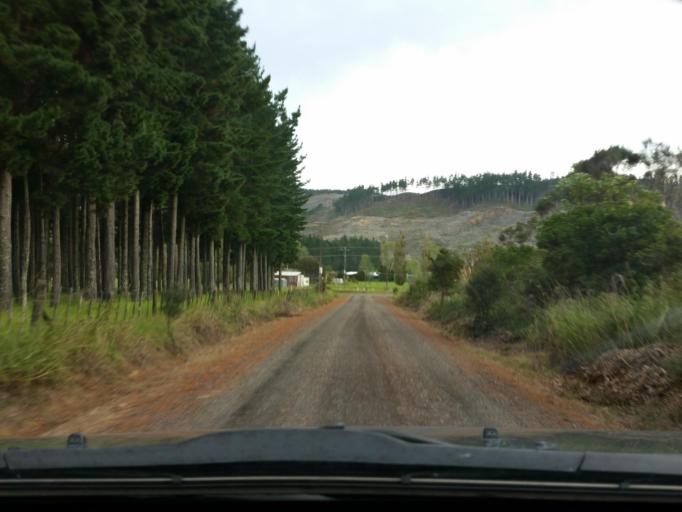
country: NZ
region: Northland
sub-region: Kaipara District
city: Dargaville
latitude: -35.7761
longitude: 173.7141
